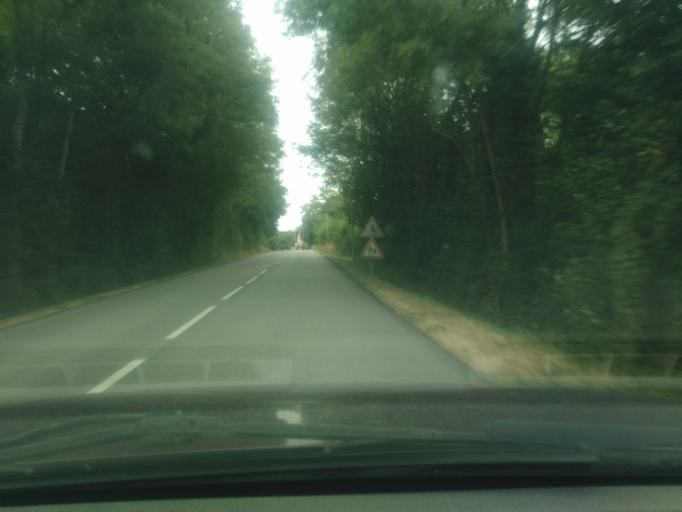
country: FR
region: Bourgogne
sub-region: Departement de la Nievre
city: Dornes
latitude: 46.7710
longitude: 3.3128
